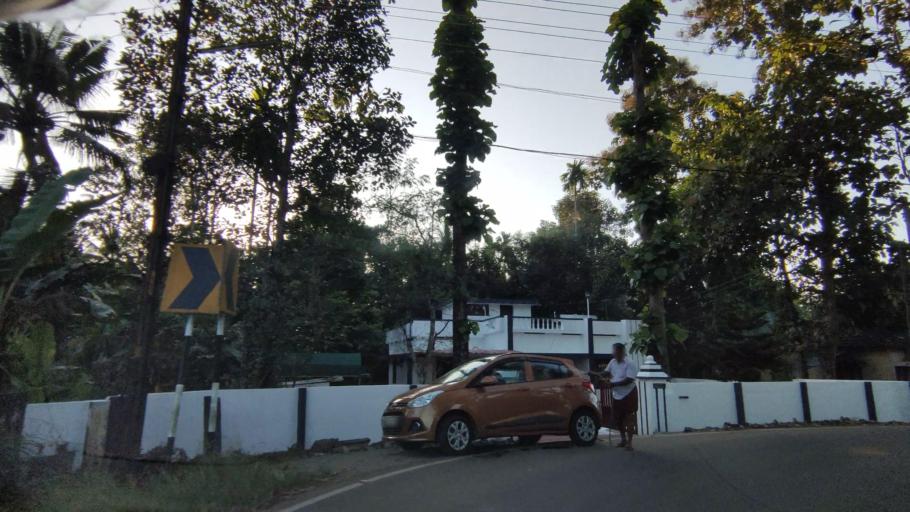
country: IN
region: Kerala
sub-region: Kottayam
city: Kottayam
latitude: 9.6215
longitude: 76.4929
